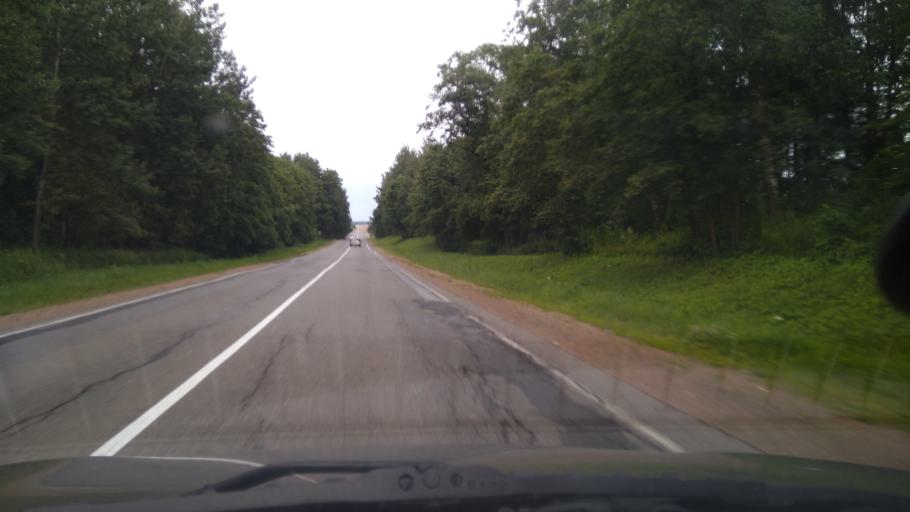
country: BY
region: Minsk
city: Bal'shavik
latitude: 53.9841
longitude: 27.5477
